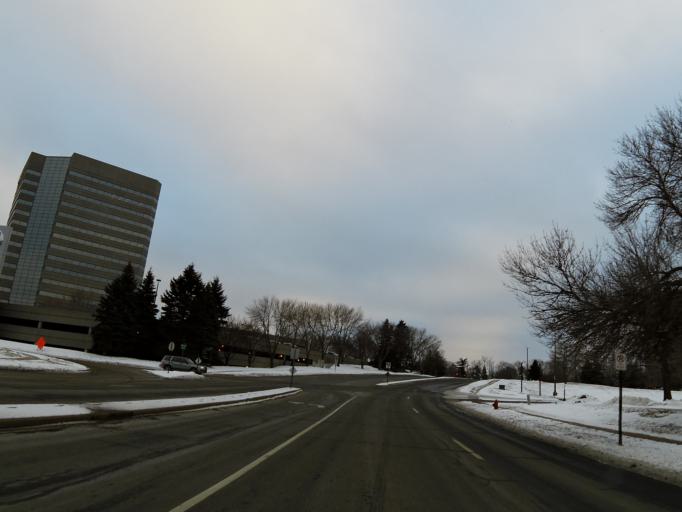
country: US
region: Minnesota
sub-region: Hennepin County
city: Bloomington
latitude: 44.8577
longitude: -93.3018
